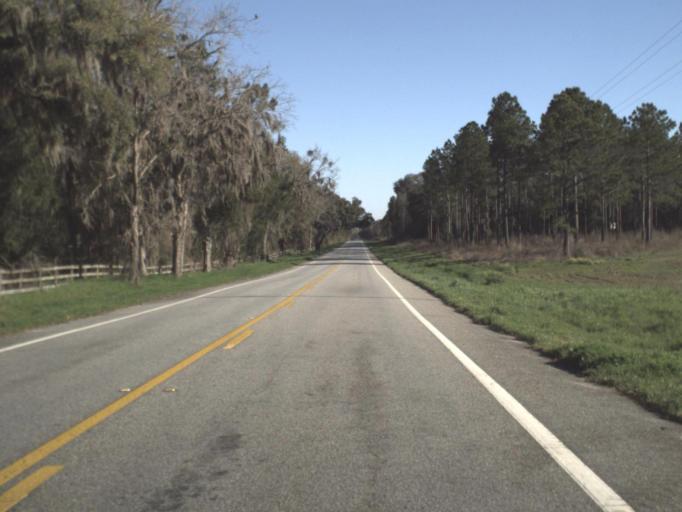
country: US
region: Georgia
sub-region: Brooks County
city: Quitman
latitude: 30.6377
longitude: -83.6446
